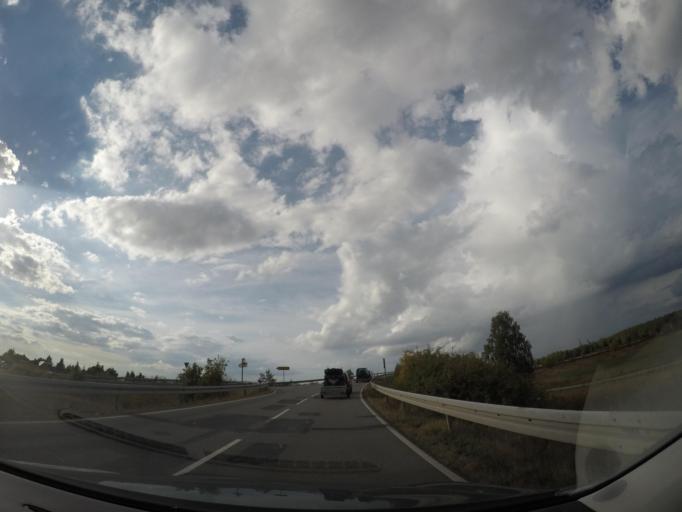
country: DE
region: Saxony-Anhalt
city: Mieste
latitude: 52.4887
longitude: 11.2390
